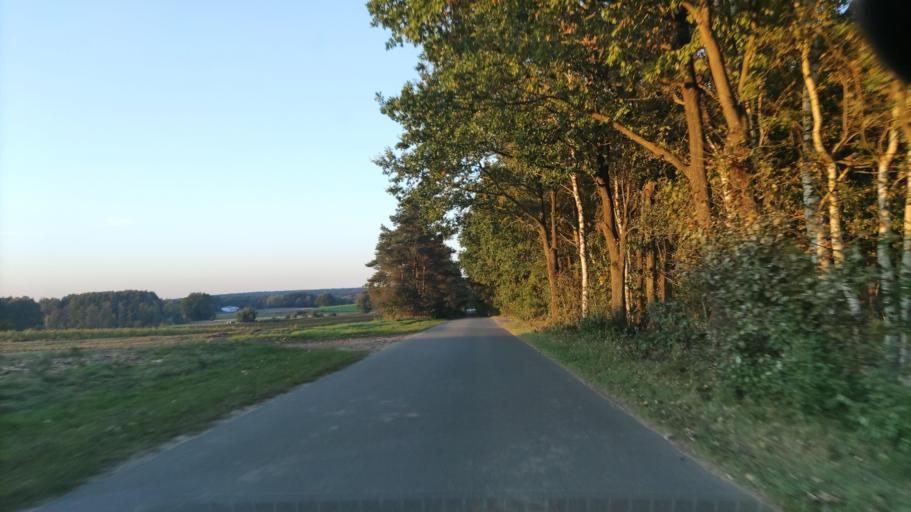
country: DE
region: Lower Saxony
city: Bispingen
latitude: 53.0826
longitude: 10.0188
